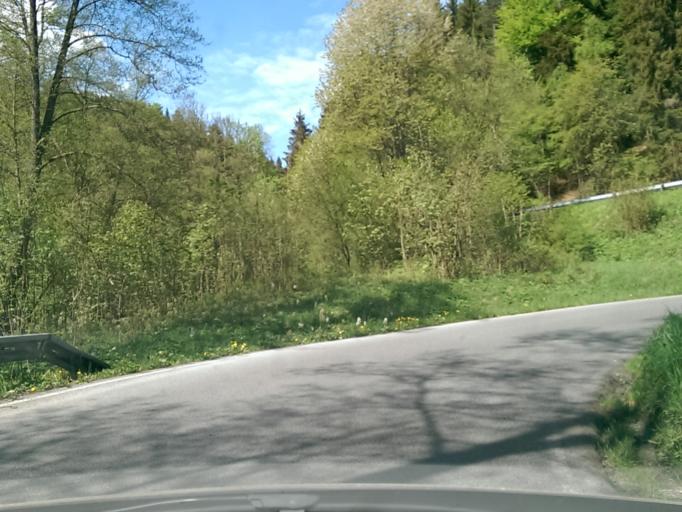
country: CZ
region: Liberecky
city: Mala Skala
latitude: 50.6583
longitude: 15.2153
